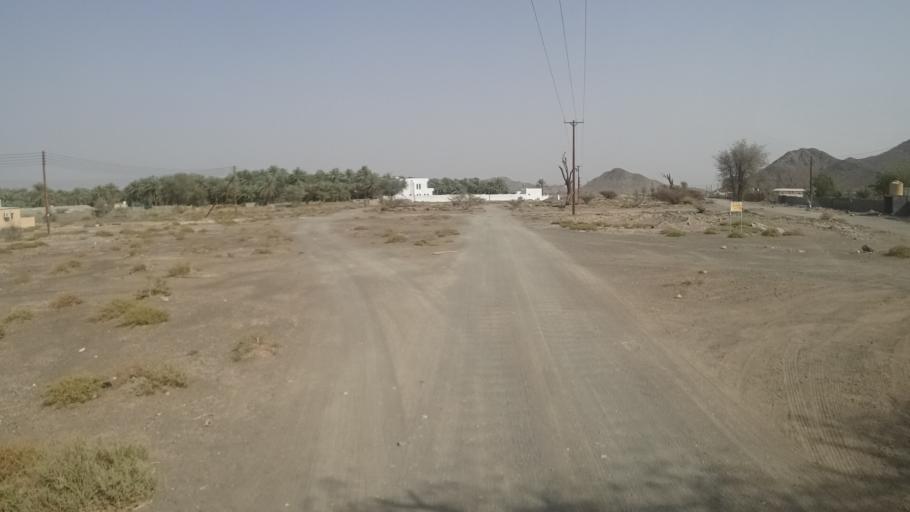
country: OM
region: Ash Sharqiyah
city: Ibra'
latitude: 22.7065
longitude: 58.1718
